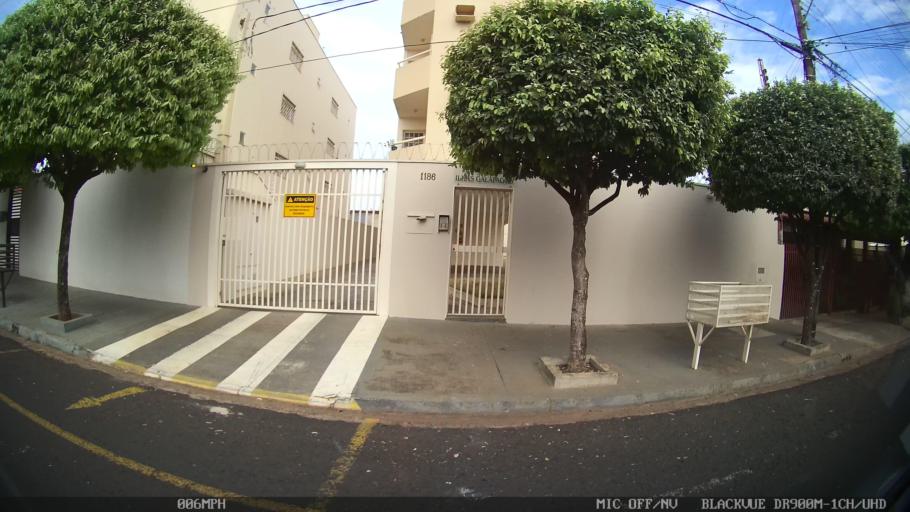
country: BR
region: Sao Paulo
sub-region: Sao Jose Do Rio Preto
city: Sao Jose do Rio Preto
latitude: -20.8315
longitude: -49.3801
